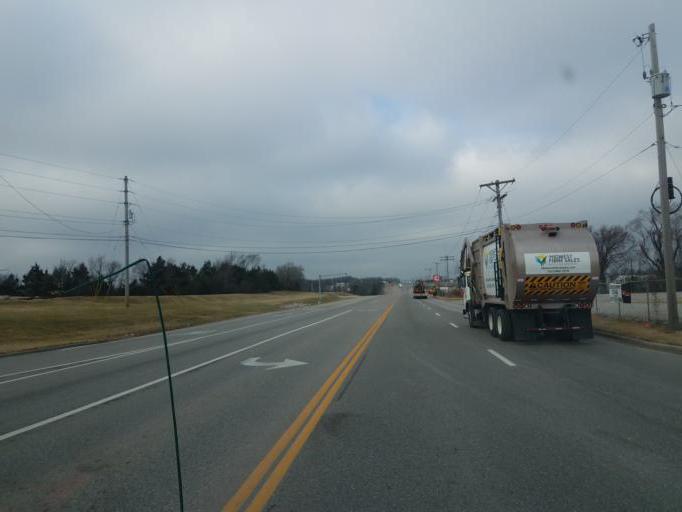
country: US
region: Missouri
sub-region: Greene County
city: Springfield
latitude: 37.2386
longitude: -93.2159
